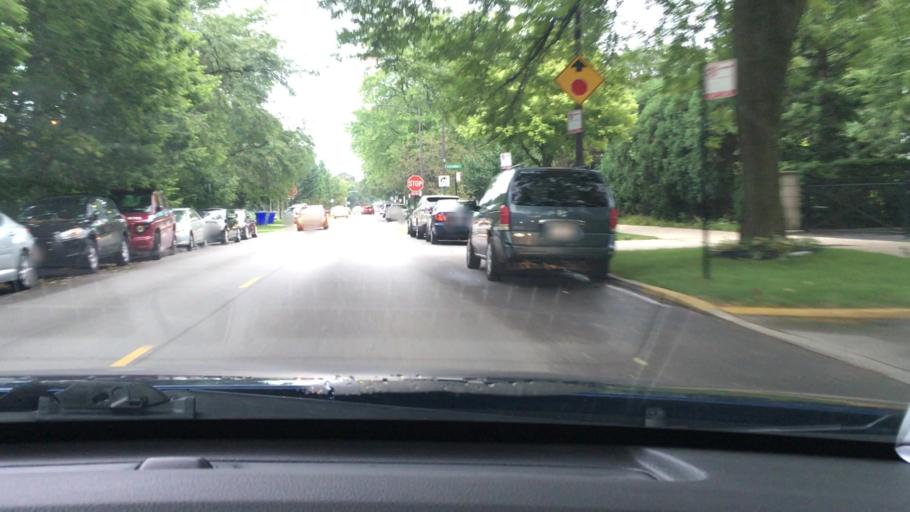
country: US
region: Illinois
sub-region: Cook County
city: Evanston
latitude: 41.9714
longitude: -87.6504
